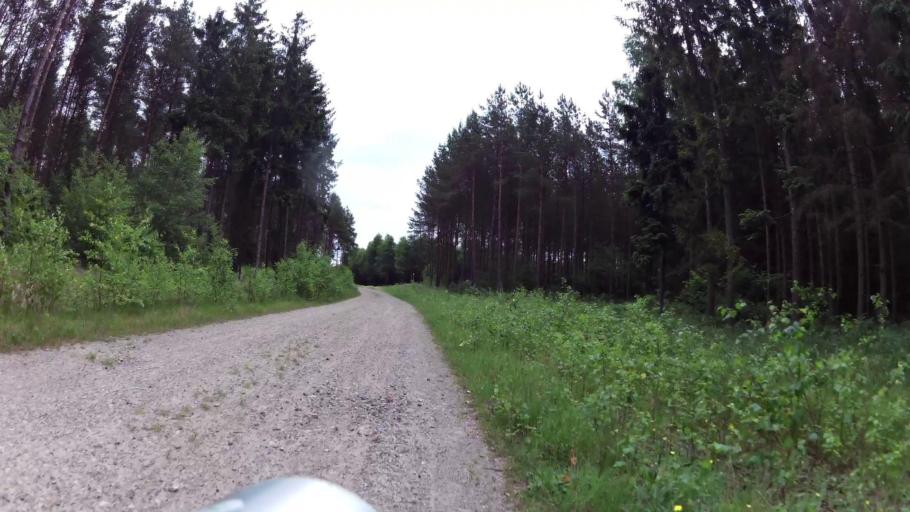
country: PL
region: West Pomeranian Voivodeship
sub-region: Powiat szczecinecki
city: Bialy Bor
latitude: 53.9207
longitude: 16.8341
